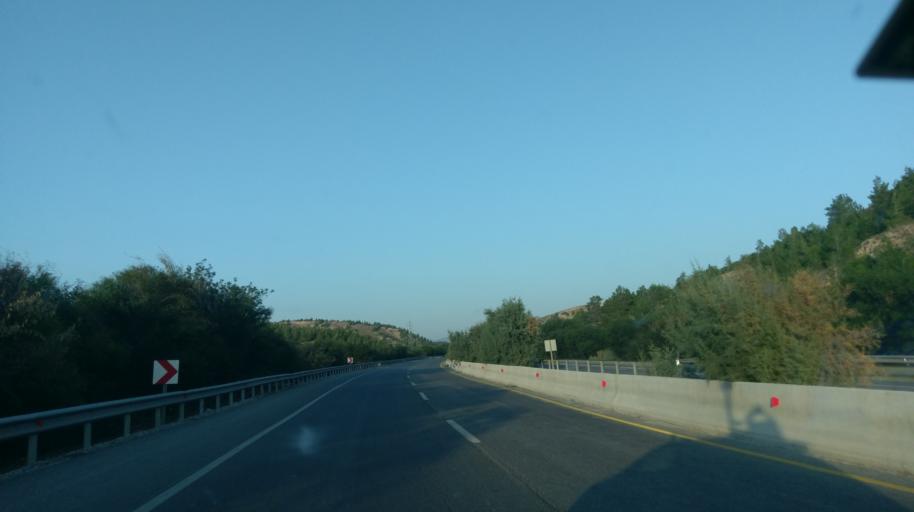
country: CY
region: Lefkosia
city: Akaki
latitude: 35.2046
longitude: 33.1173
